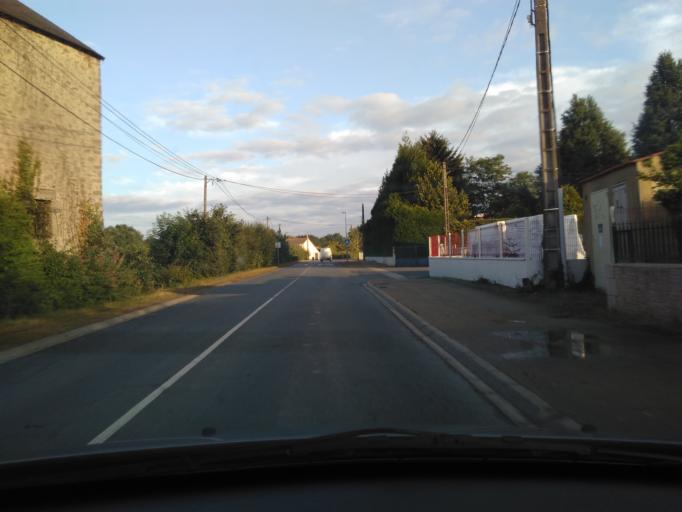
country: FR
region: Pays de la Loire
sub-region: Departement de la Vendee
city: Mouilleron-le-Captif
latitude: 46.7313
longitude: -1.4380
